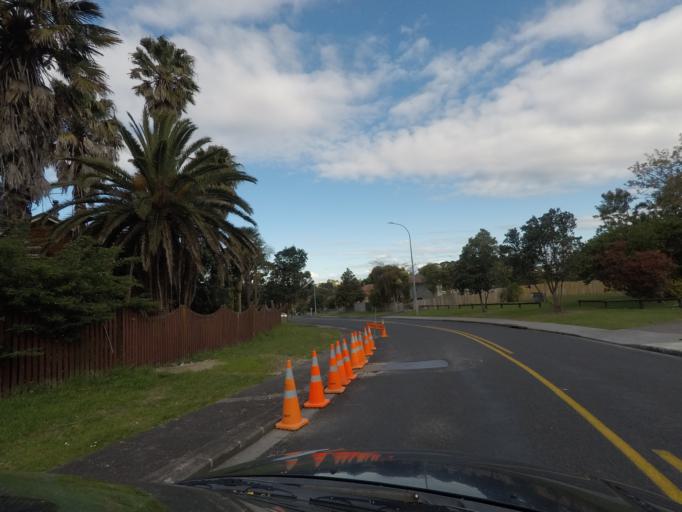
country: NZ
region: Auckland
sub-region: Auckland
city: Rosebank
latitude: -36.8857
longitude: 174.6488
